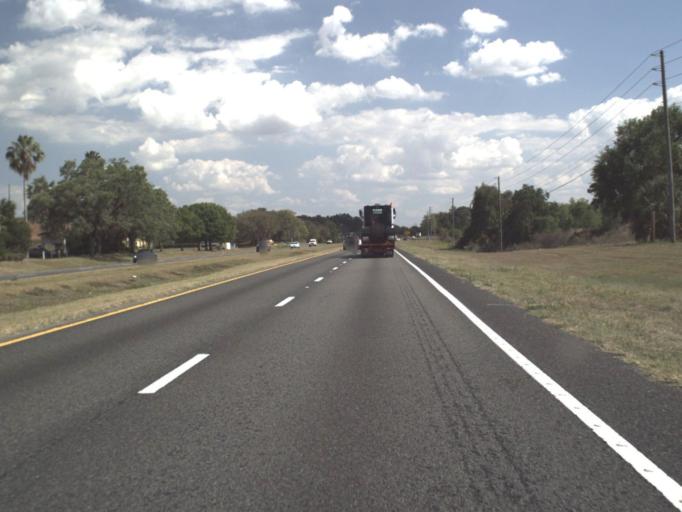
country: US
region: Florida
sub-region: Lake County
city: Hawthorne
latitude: 28.7338
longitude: -81.8680
